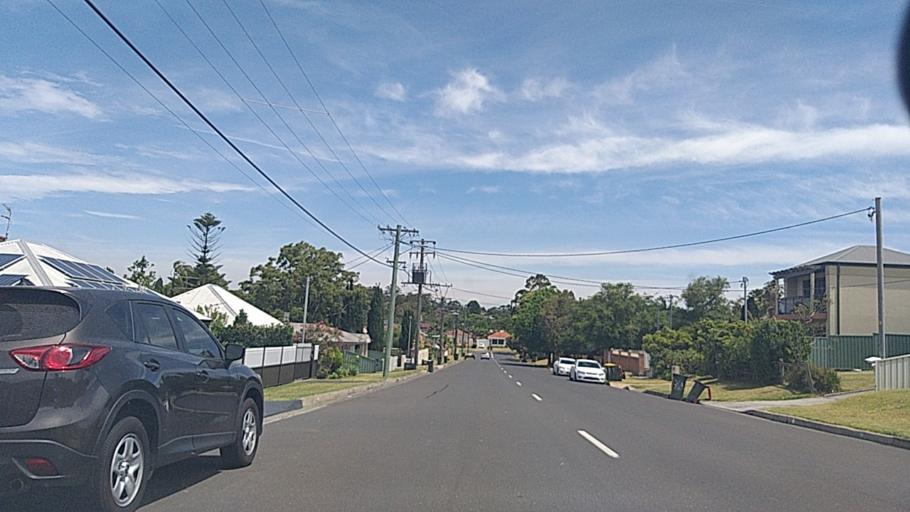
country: AU
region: New South Wales
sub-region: Wollongong
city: Mount Ousley
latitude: -34.3928
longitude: 150.8812
